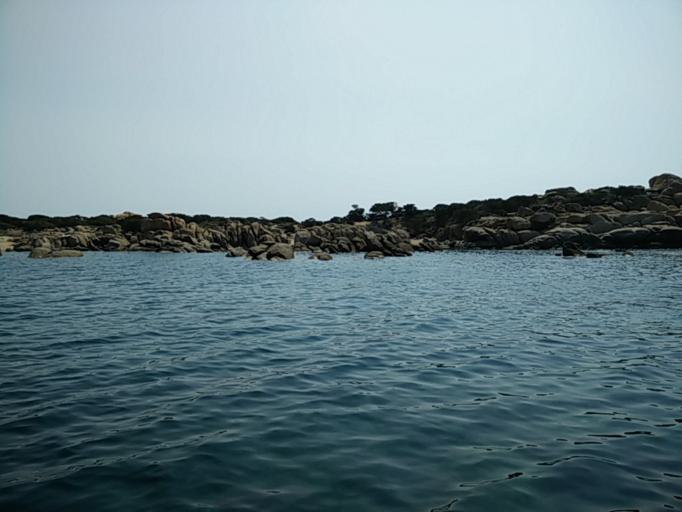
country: FR
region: Corsica
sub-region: Departement de la Corse-du-Sud
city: Propriano
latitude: 41.5646
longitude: 8.7879
